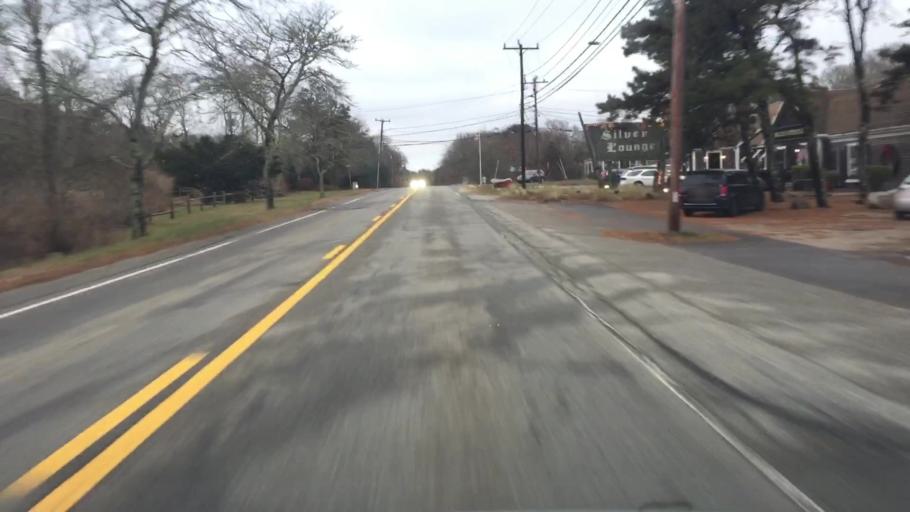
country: US
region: Massachusetts
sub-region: Barnstable County
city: North Falmouth
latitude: 41.6399
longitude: -70.6159
